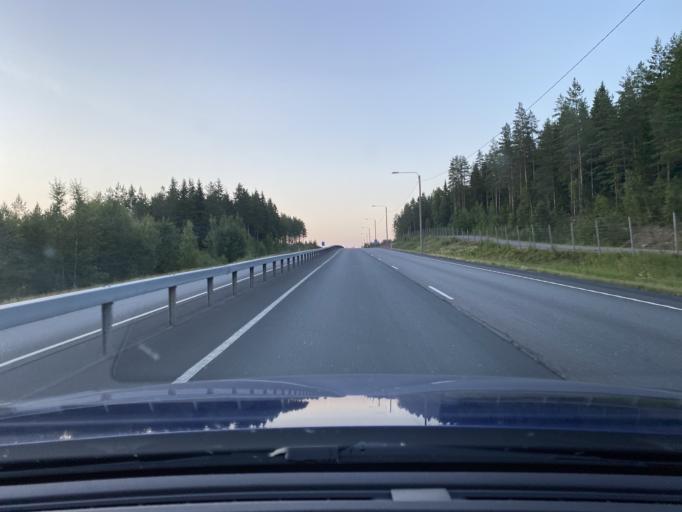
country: FI
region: Pirkanmaa
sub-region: Luoteis-Pirkanmaa
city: Parkano
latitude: 61.8886
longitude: 22.9761
